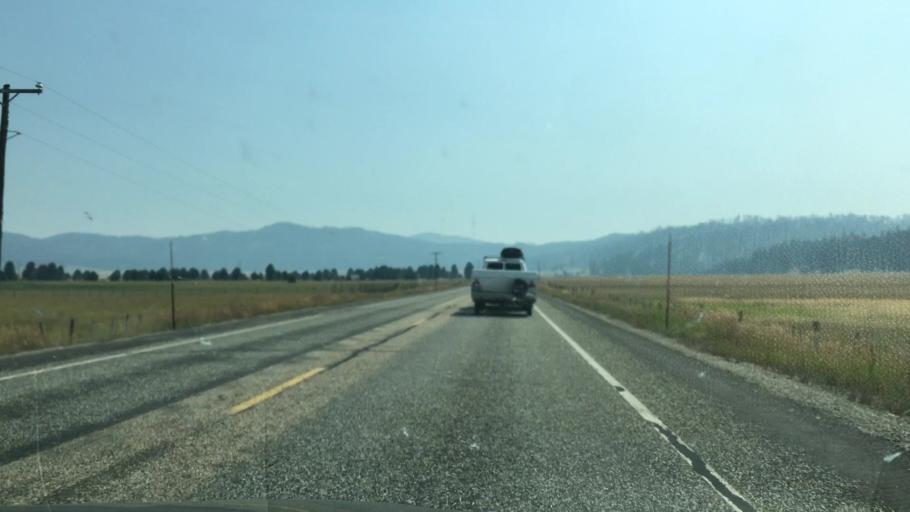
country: US
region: Idaho
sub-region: Valley County
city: Cascade
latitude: 44.3492
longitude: -116.0258
